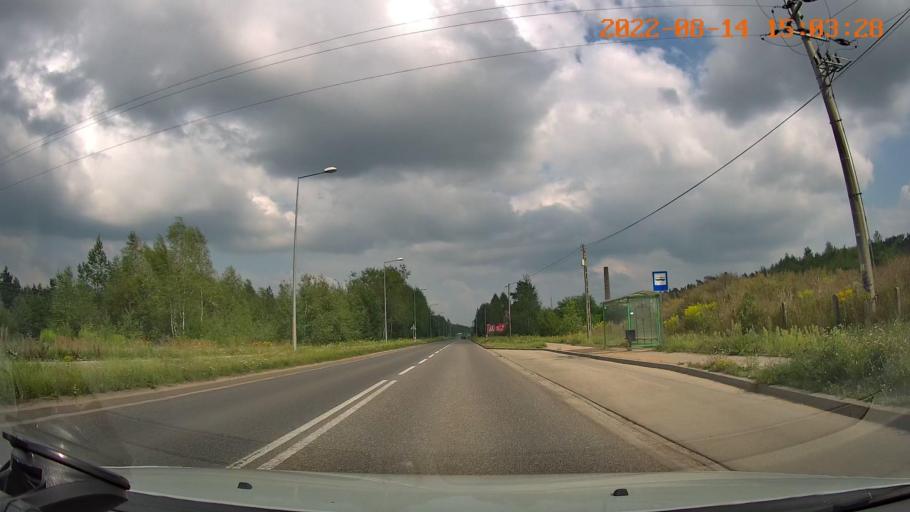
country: PL
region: Swietokrzyskie
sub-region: Powiat kielecki
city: Kostomloty Drugie
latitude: 50.8822
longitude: 20.5354
